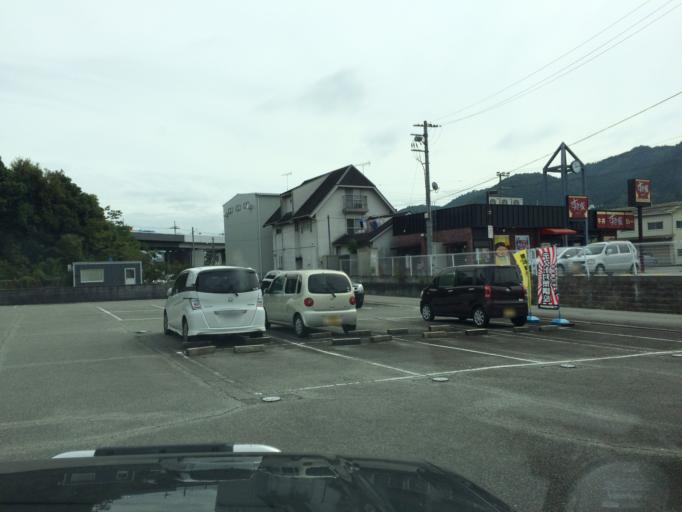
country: JP
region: Hyogo
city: Sasayama
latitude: 35.0649
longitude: 135.1808
